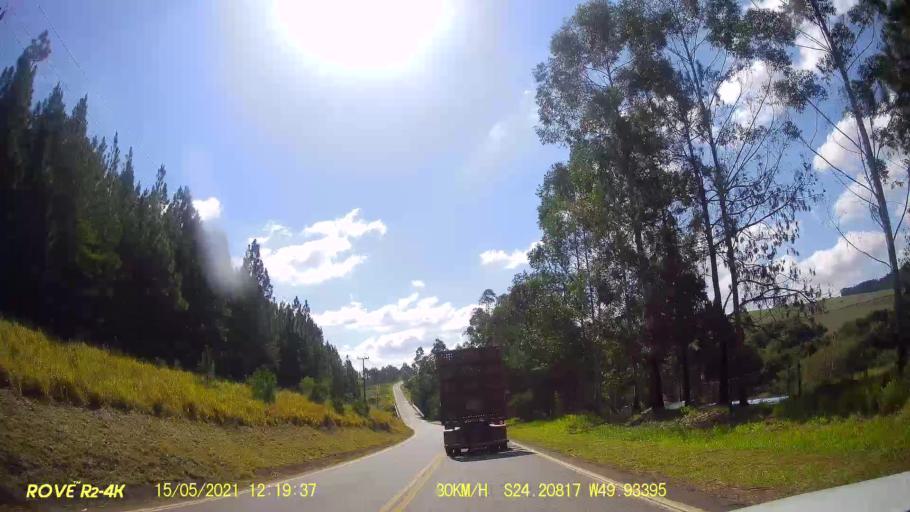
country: BR
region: Parana
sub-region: Jaguariaiva
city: Jaguariaiva
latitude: -24.2078
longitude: -49.9338
